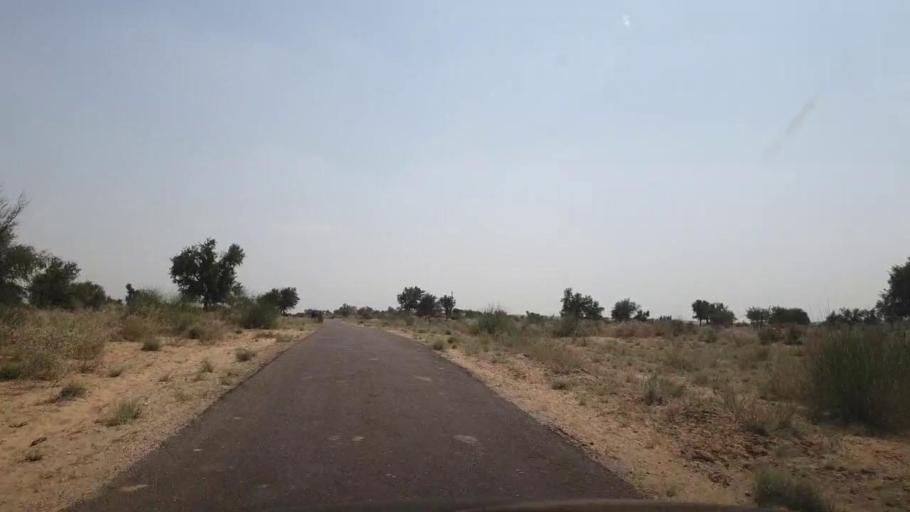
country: PK
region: Sindh
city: Islamkot
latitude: 25.1000
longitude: 70.7262
